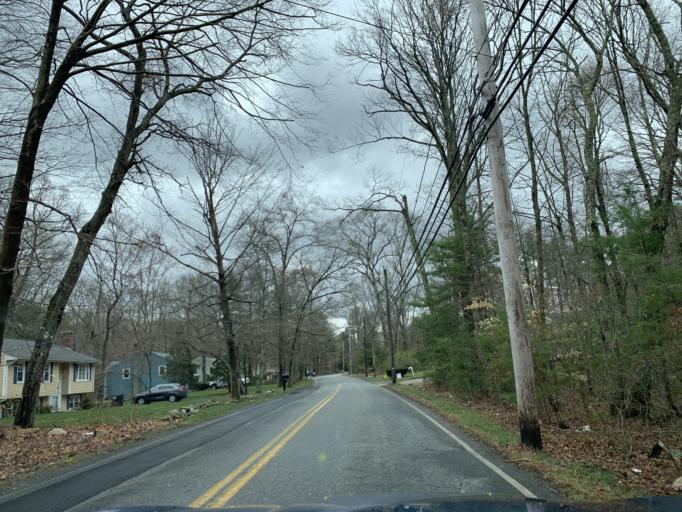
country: US
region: Massachusetts
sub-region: Bristol County
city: Norton
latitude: 41.9406
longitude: -71.2205
